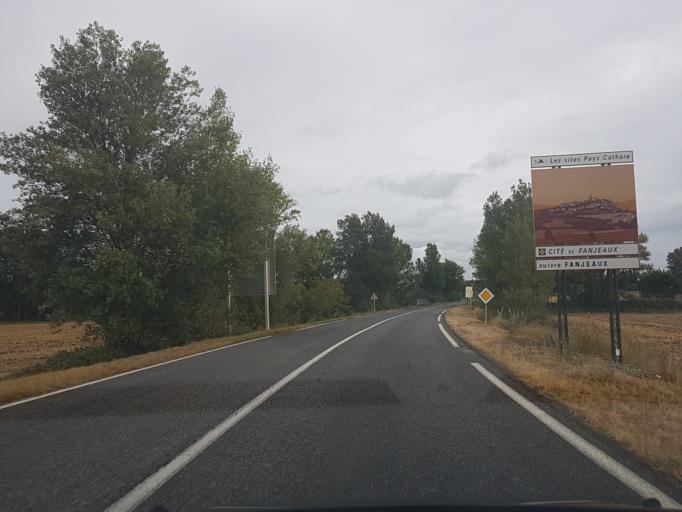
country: FR
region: Languedoc-Roussillon
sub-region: Departement de l'Aude
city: Bram
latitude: 43.2403
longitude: 2.1024
